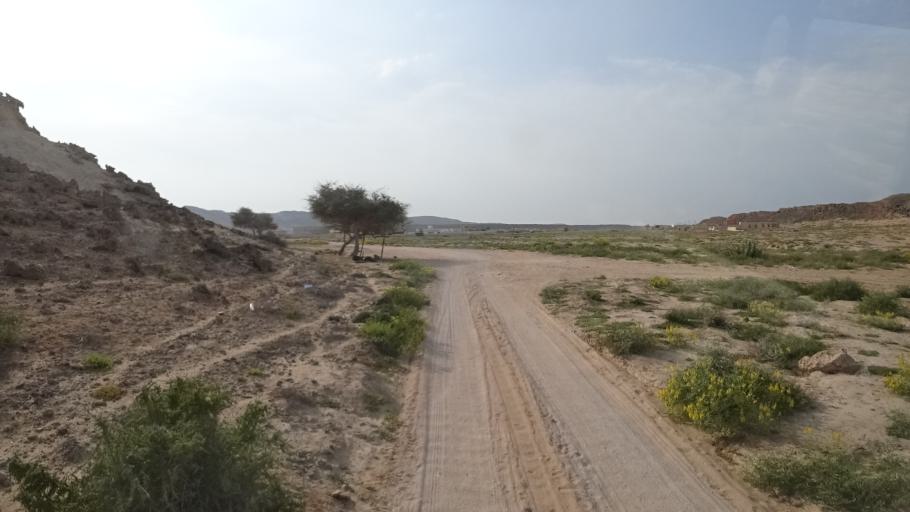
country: OM
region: Ash Sharqiyah
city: Sur
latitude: 22.4314
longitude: 59.8313
